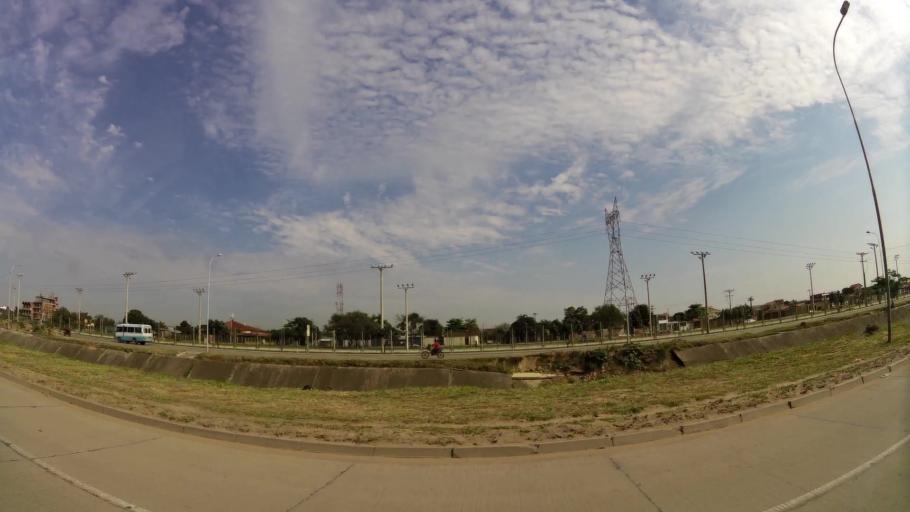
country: BO
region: Santa Cruz
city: Santa Cruz de la Sierra
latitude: -17.7342
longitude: -63.1395
